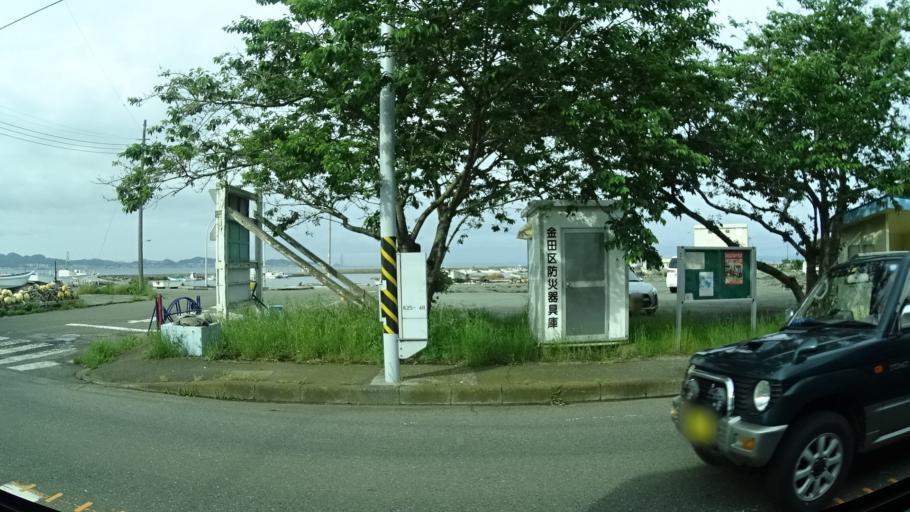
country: JP
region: Kanagawa
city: Miura
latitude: 35.1585
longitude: 139.6639
